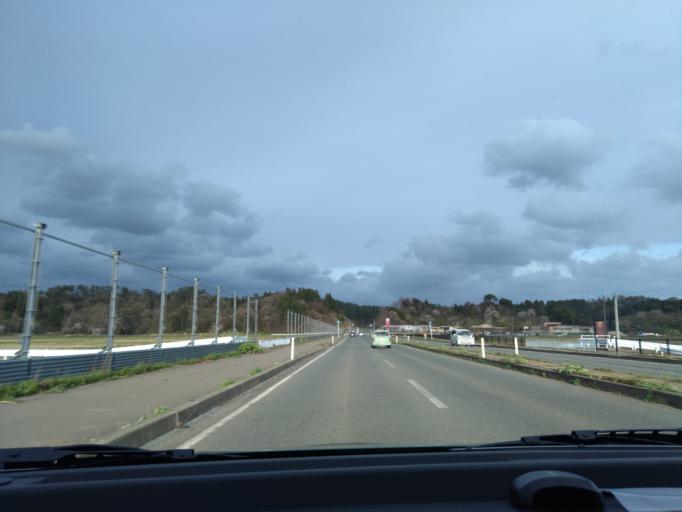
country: JP
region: Akita
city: Akita Shi
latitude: 39.7526
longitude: 140.1133
